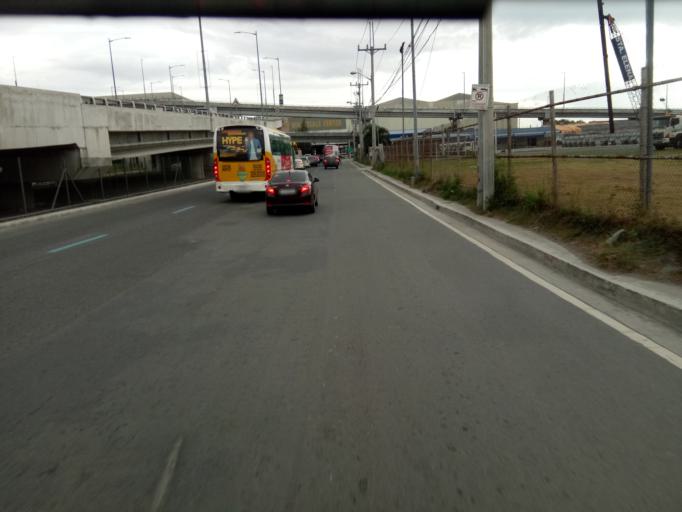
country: PH
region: Metro Manila
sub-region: Makati City
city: Makati City
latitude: 14.5191
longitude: 120.9906
